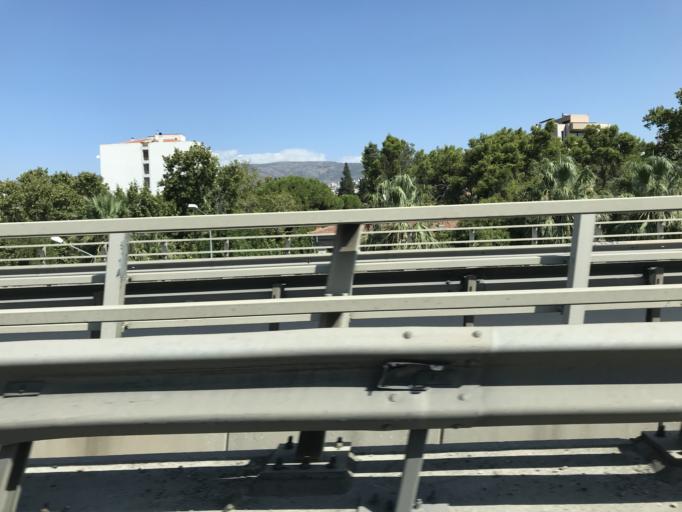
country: TR
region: Izmir
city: Bornova
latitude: 38.4590
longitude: 27.2166
